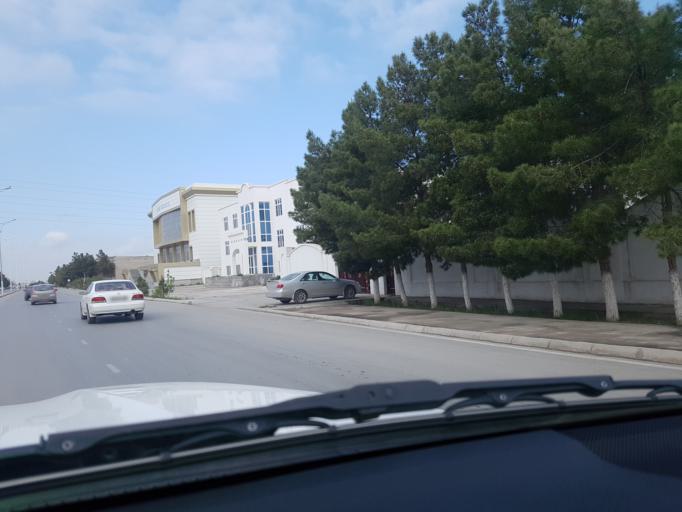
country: TM
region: Lebap
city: Turkmenabat
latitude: 39.0726
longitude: 63.5930
